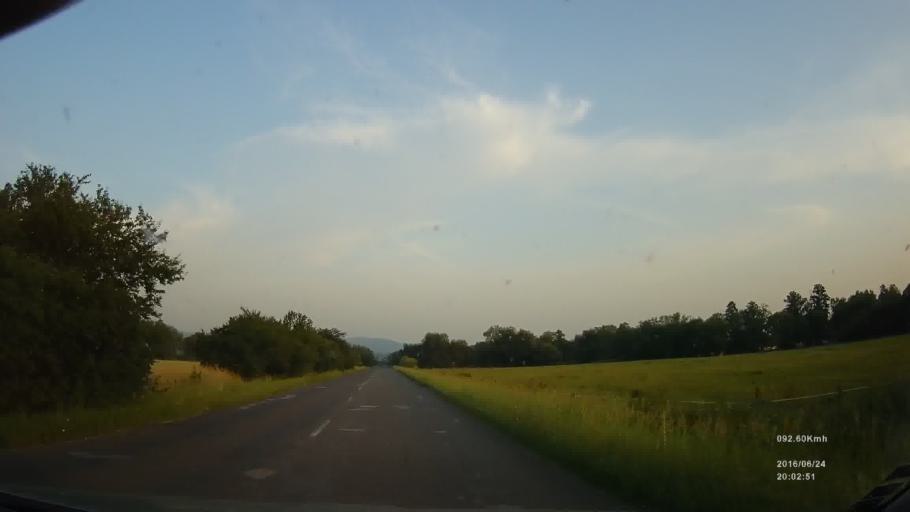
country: SK
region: Banskobystricky
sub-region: Okres Banska Bystrica
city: Zvolen
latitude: 48.6234
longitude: 19.1271
